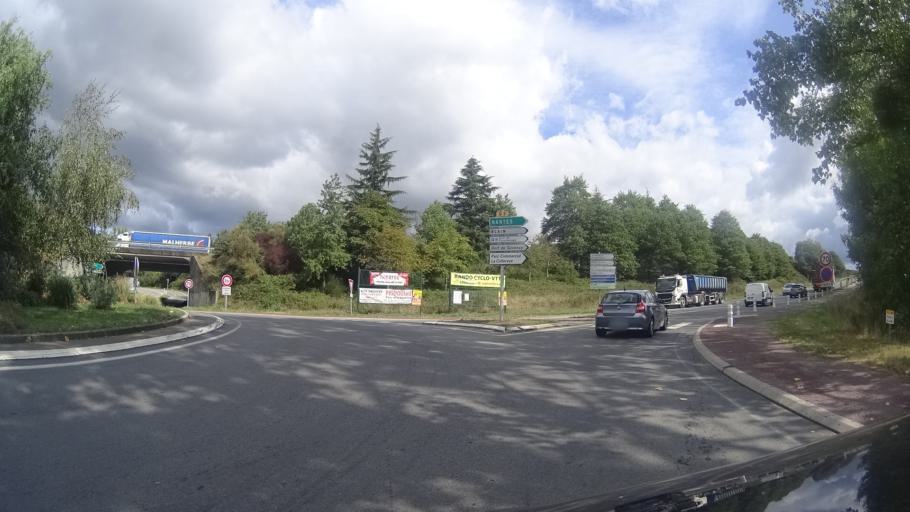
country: FR
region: Pays de la Loire
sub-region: Departement de la Loire-Atlantique
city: Savenay
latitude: 47.3624
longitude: -1.9568
